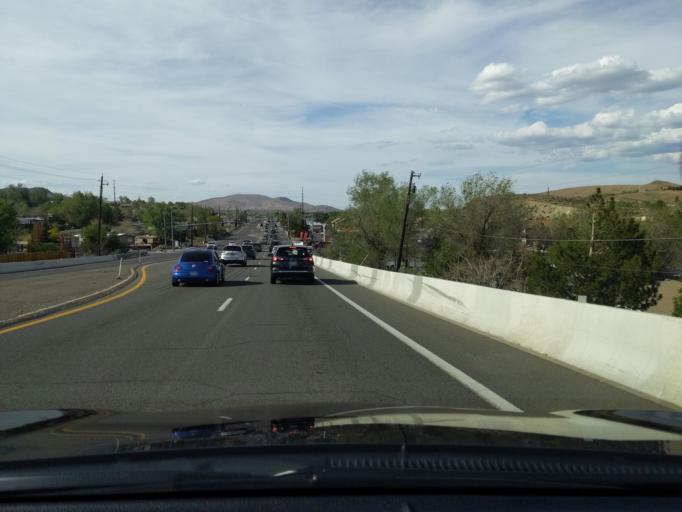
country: US
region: Nevada
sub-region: Washoe County
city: Sun Valley
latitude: 39.5692
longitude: -119.7821
